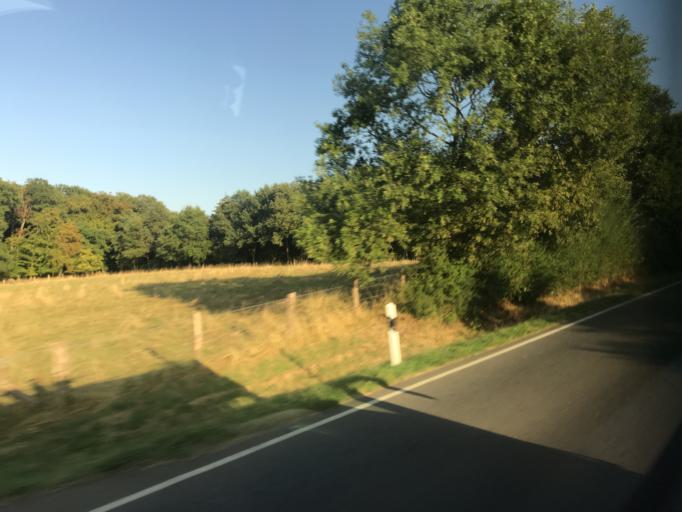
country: LU
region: Luxembourg
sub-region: Canton d'Esch-sur-Alzette
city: Frisange
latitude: 49.5289
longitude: 6.1821
